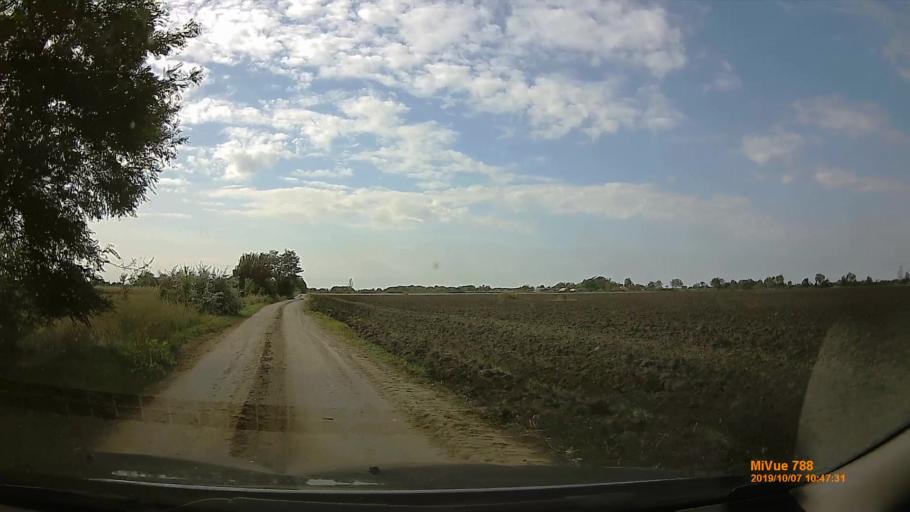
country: HU
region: Bekes
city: Kondoros
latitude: 46.7347
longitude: 20.8152
